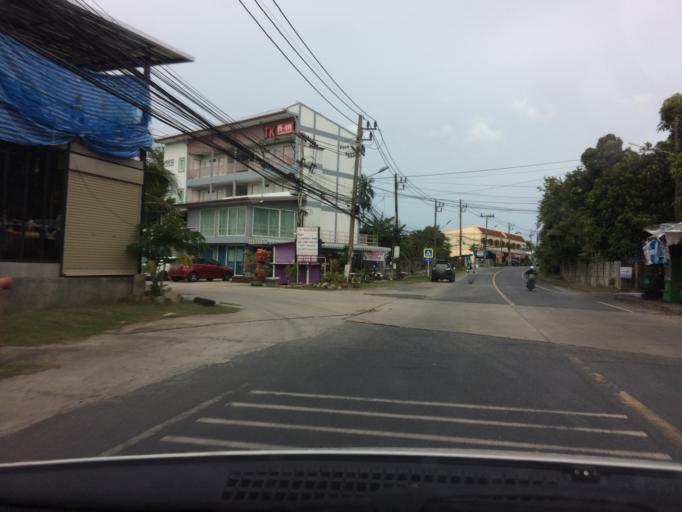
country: TH
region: Phuket
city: Ban Ratsada
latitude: 7.9064
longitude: 98.4059
